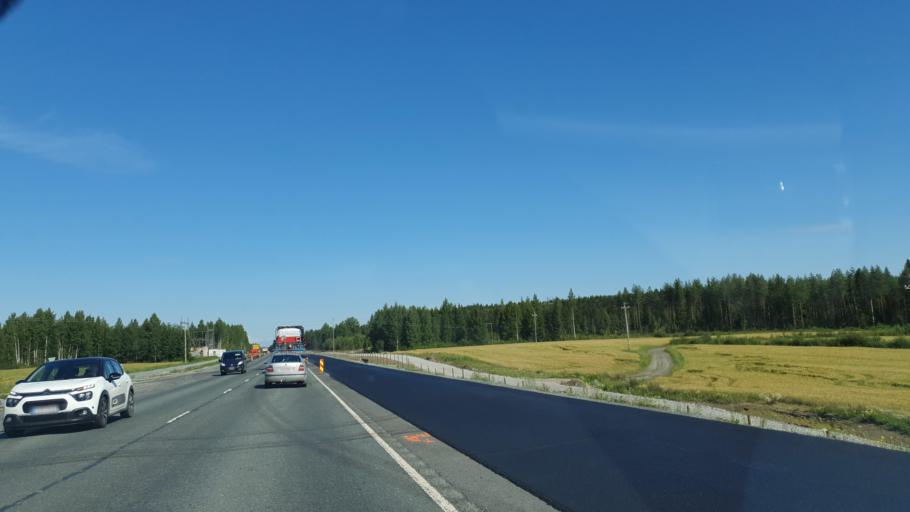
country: FI
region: Northern Savo
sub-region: Ylae-Savo
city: Lapinlahti
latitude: 63.2871
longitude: 27.4549
